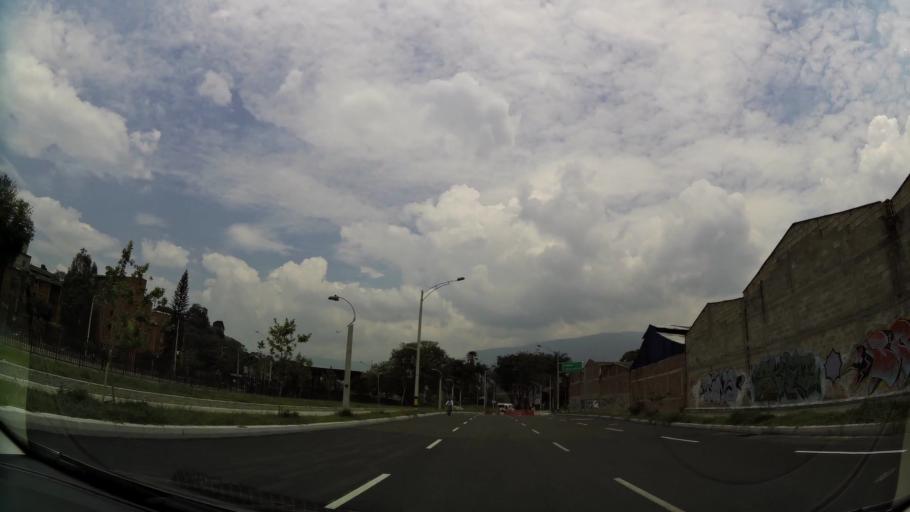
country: CO
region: Antioquia
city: Itagui
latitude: 6.1767
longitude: -75.6046
